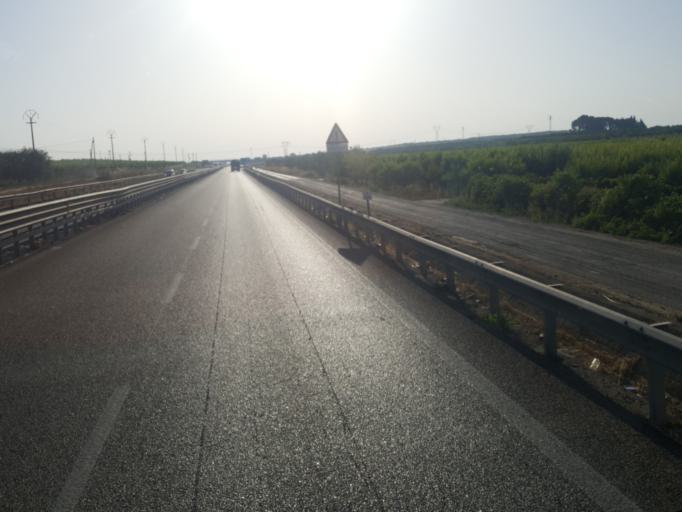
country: IT
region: Apulia
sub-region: Provincia di Barletta - Andria - Trani
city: San Ferdinando di Puglia
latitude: 41.2804
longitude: 15.9904
